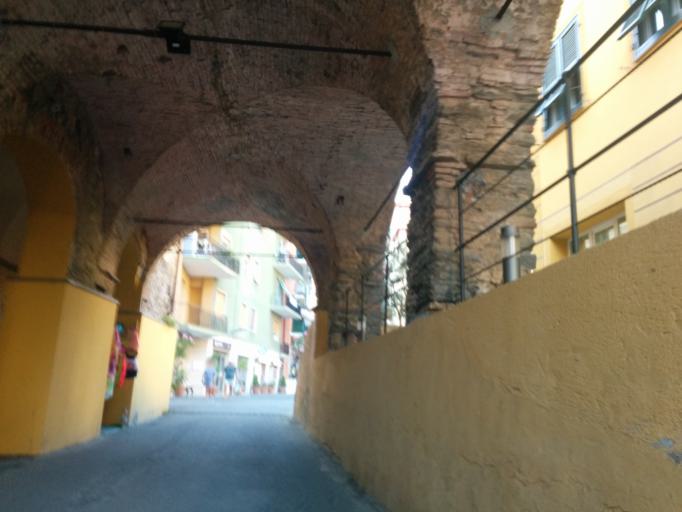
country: IT
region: Liguria
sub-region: Provincia di La Spezia
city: Monterosso al Mare
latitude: 44.1481
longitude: 9.6549
